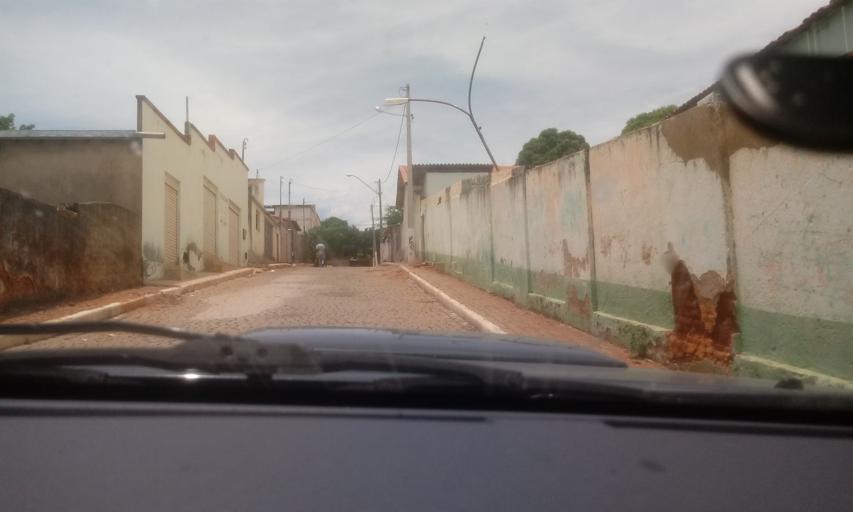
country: BR
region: Bahia
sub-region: Riacho De Santana
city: Riacho de Santana
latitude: -13.6093
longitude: -42.9388
